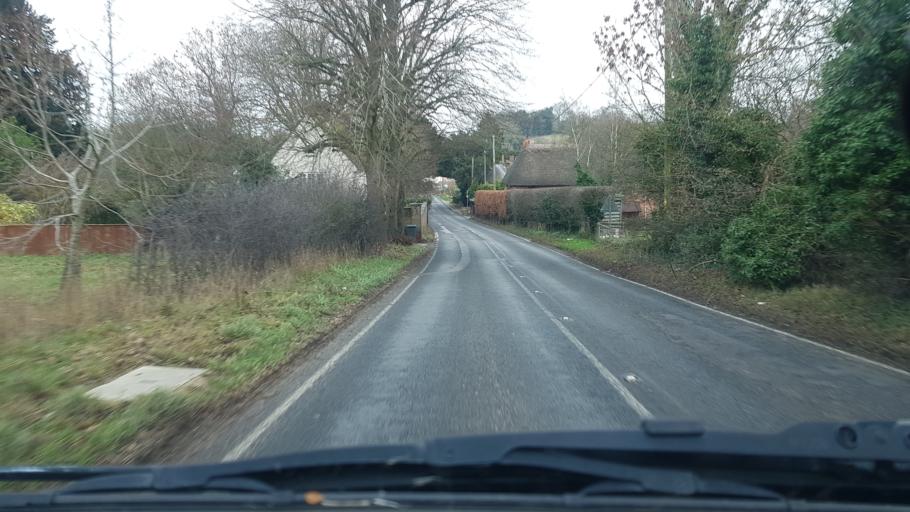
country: GB
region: England
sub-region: Hampshire
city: Andover
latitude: 51.2750
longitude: -1.4554
